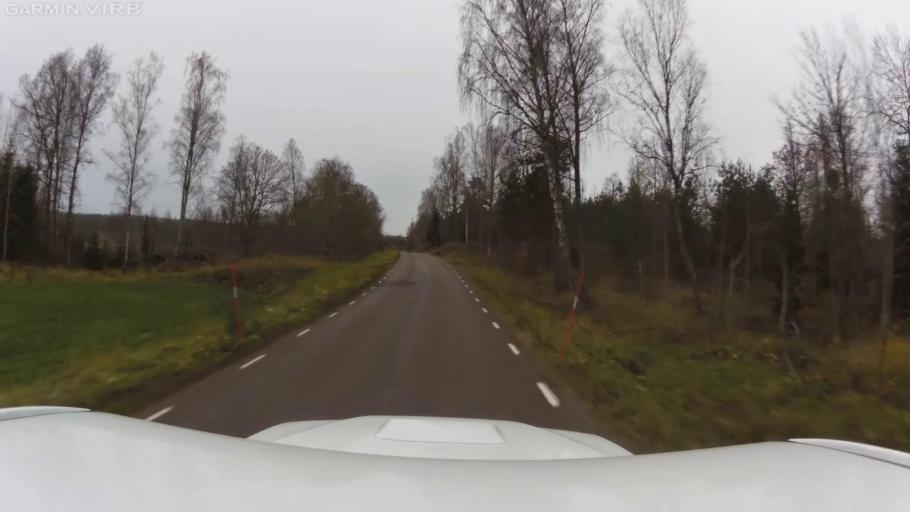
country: SE
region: OEstergoetland
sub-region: Mjolby Kommun
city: Mantorp
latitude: 58.1596
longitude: 15.3911
